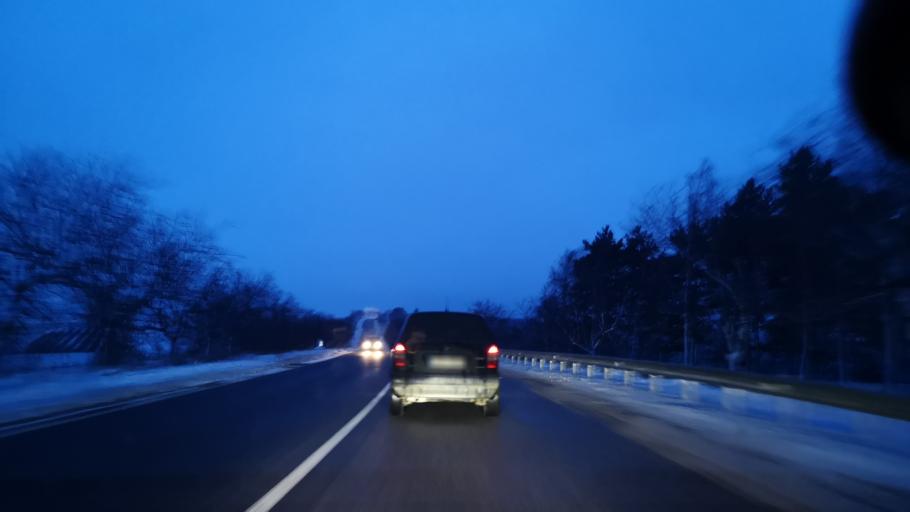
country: MD
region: Orhei
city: Orhei
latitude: 47.5661
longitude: 28.7966
